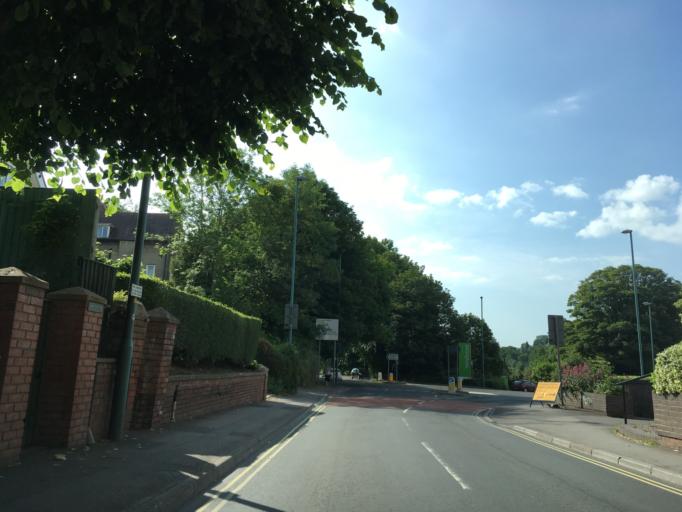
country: GB
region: England
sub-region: Gloucestershire
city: Stroud
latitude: 51.7430
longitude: -2.2150
